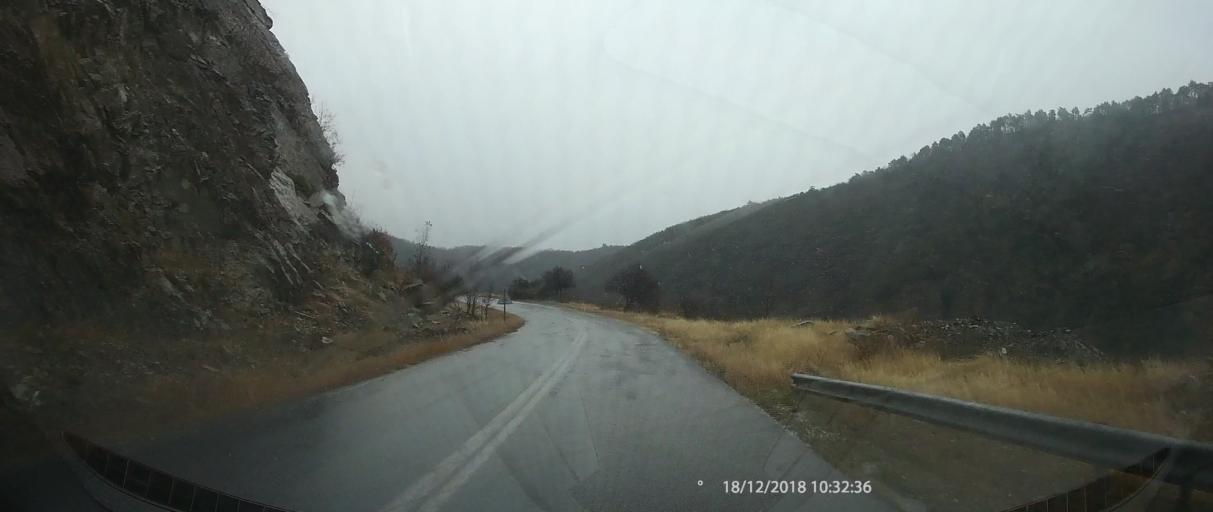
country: GR
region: Central Macedonia
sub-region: Nomos Pierias
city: Kato Milia
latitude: 40.1921
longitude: 22.2933
